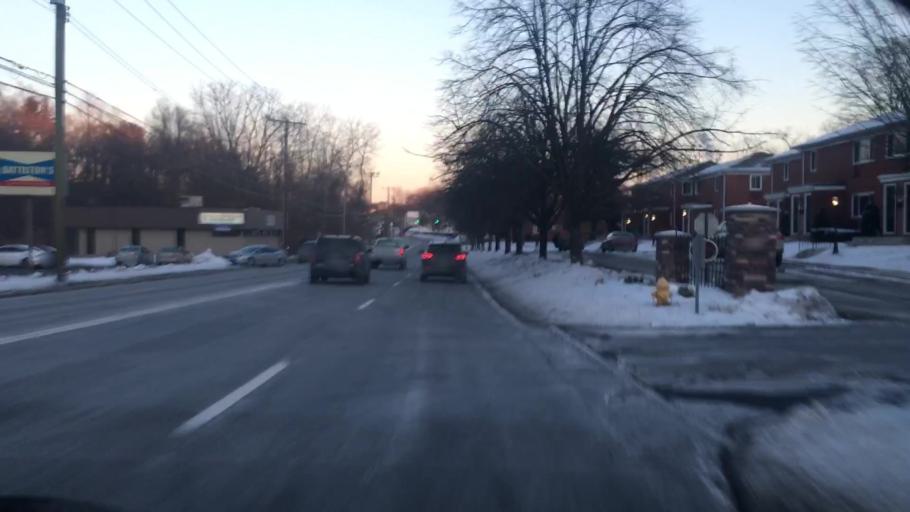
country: US
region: Connecticut
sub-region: Hartford County
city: Manchester
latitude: 41.7808
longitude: -72.5446
